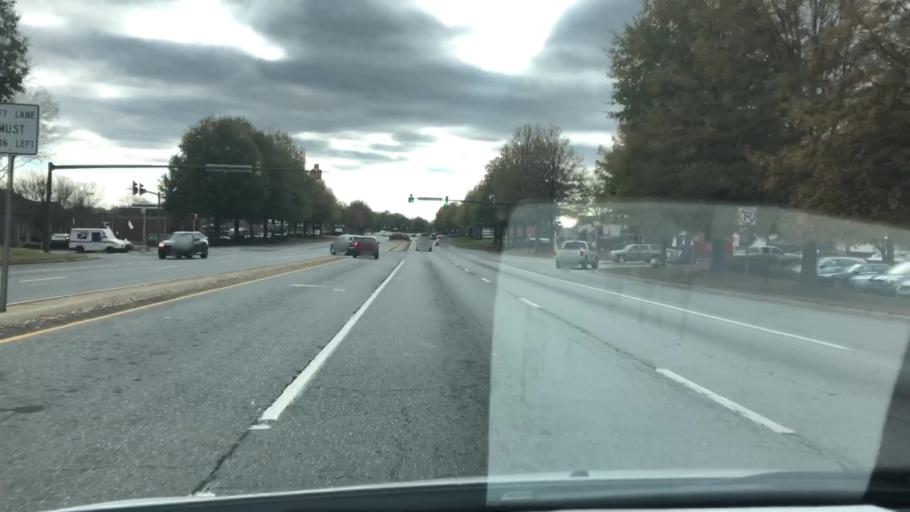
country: US
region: Georgia
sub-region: Fulton County
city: Johns Creek
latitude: 34.0728
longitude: -84.1663
